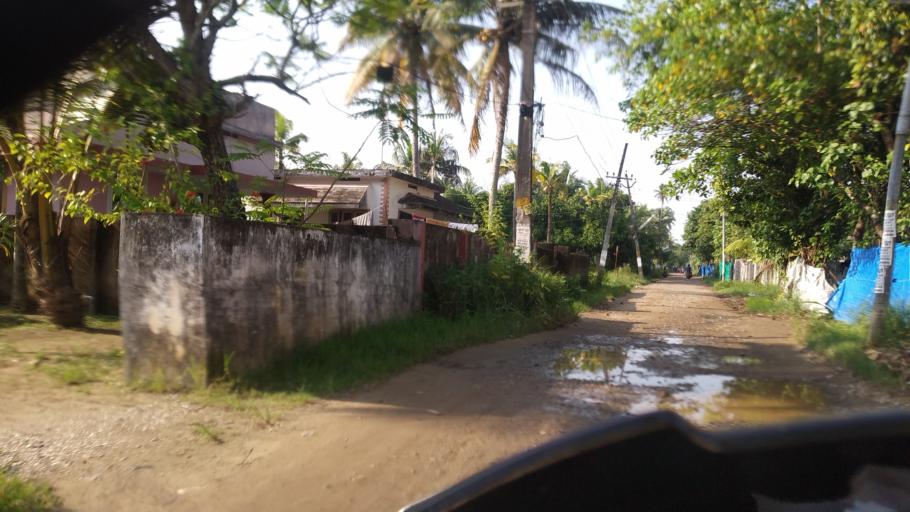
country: IN
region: Kerala
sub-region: Ernakulam
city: Cochin
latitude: 10.0095
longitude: 76.2185
